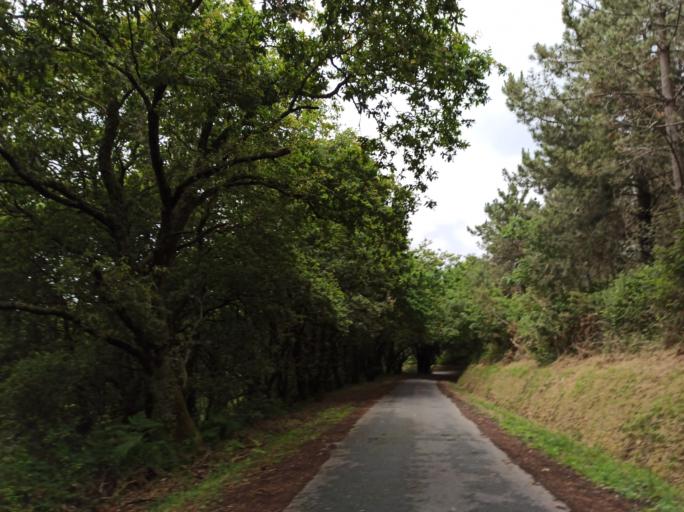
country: ES
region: Galicia
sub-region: Provincia de Pontevedra
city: Silleda
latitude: 42.7698
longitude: -8.1633
